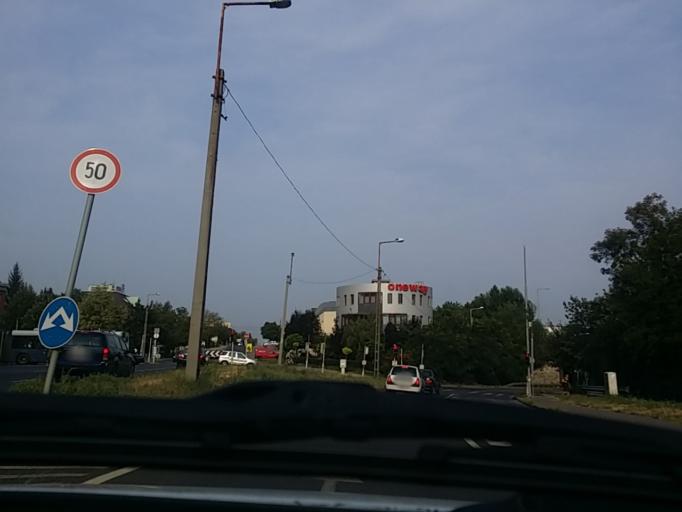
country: HU
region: Budapest
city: Budapest XII. keruelet
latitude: 47.4622
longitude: 19.0048
